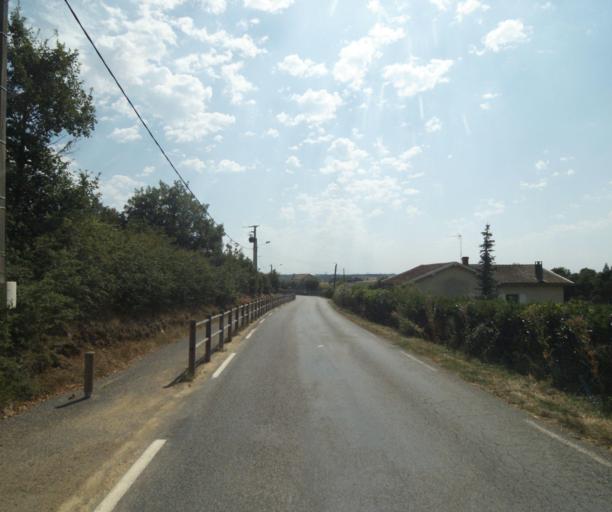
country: FR
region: Rhone-Alpes
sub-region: Departement du Rhone
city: Lentilly
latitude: 45.8414
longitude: 4.6570
